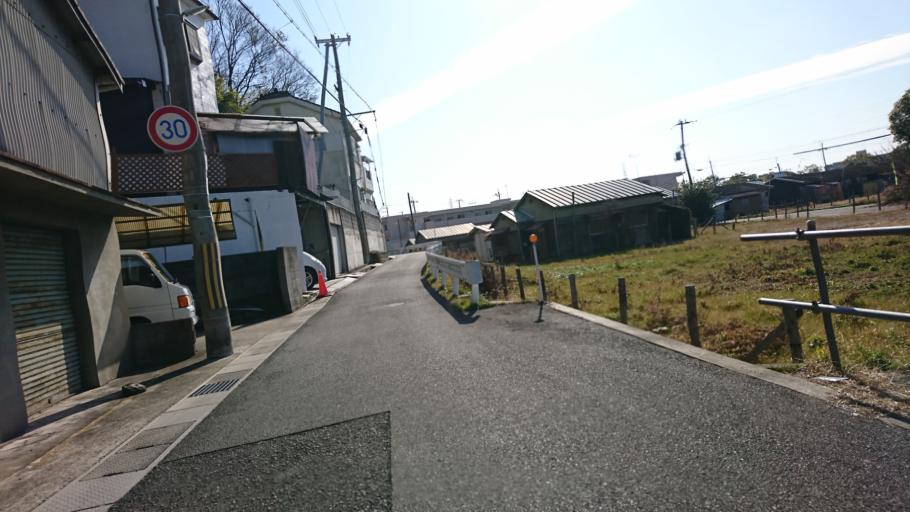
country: JP
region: Hyogo
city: Kakogawacho-honmachi
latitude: 34.7832
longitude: 134.7872
